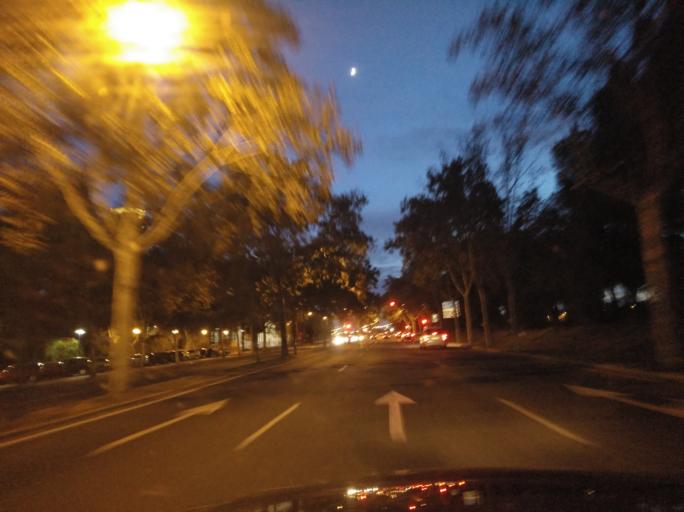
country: ES
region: Andalusia
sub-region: Provincia de Sevilla
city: Camas
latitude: 37.3973
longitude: -6.0123
